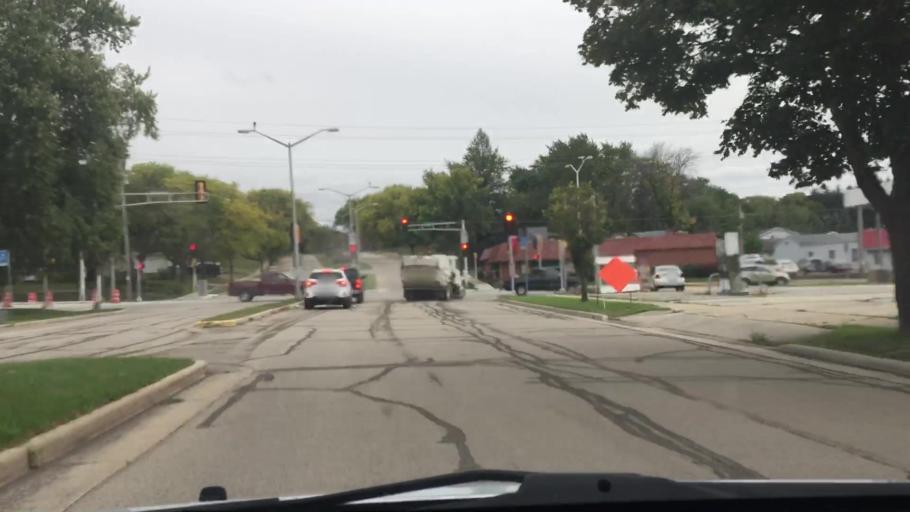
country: US
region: Wisconsin
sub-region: Waukesha County
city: Waukesha
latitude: 42.9889
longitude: -88.2323
